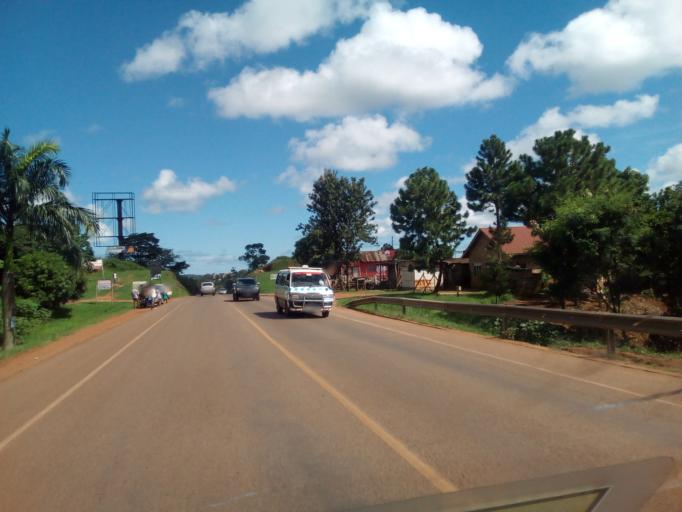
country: UG
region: Central Region
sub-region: Wakiso District
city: Kajansi
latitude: 0.1592
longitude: 32.5457
